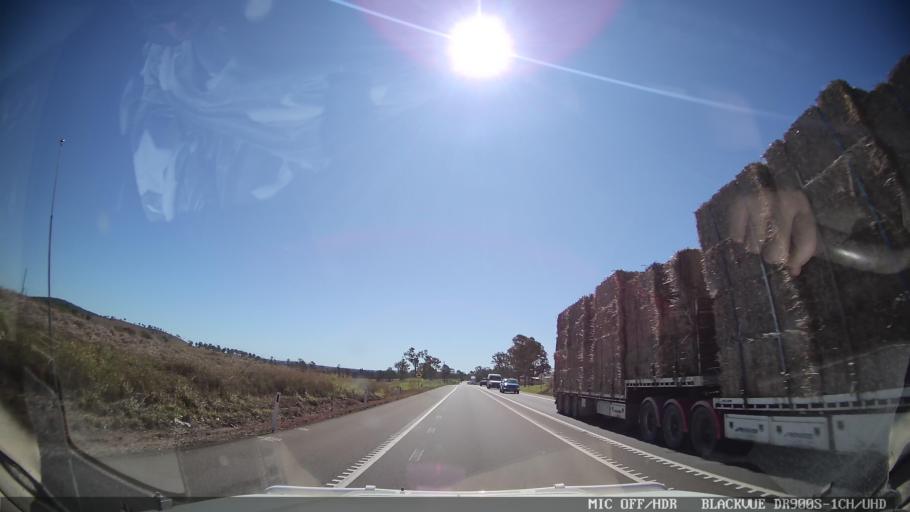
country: AU
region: Queensland
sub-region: Fraser Coast
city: Maryborough
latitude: -25.7818
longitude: 152.5962
